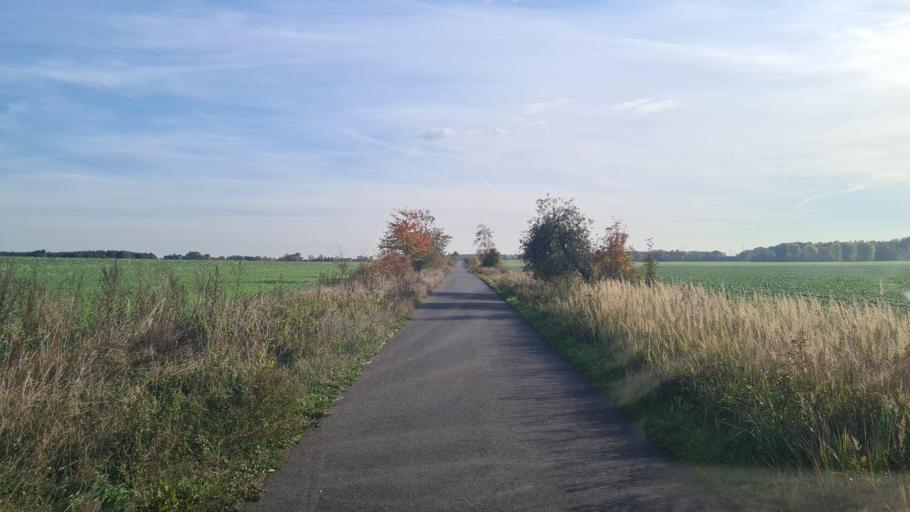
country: DE
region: Brandenburg
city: Dahme
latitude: 51.8975
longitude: 13.3898
